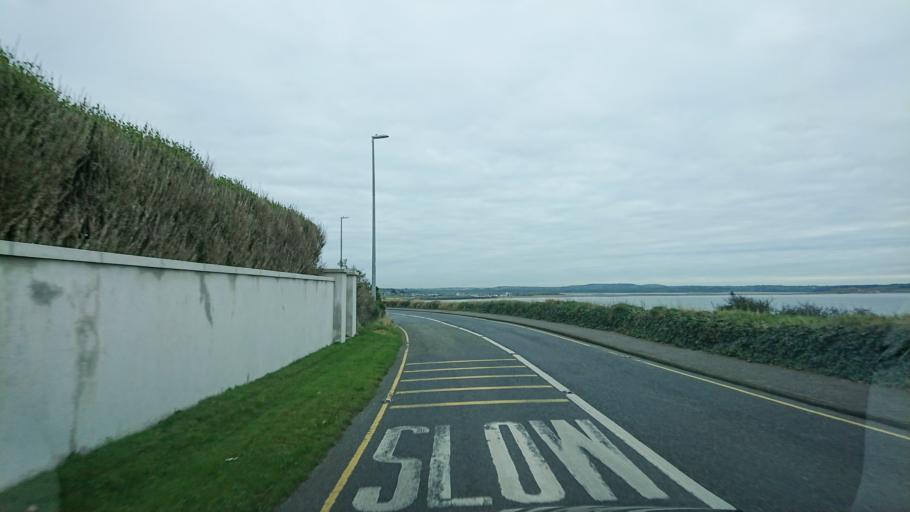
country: IE
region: Munster
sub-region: Waterford
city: Tra Mhor
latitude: 52.1516
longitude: -7.1611
